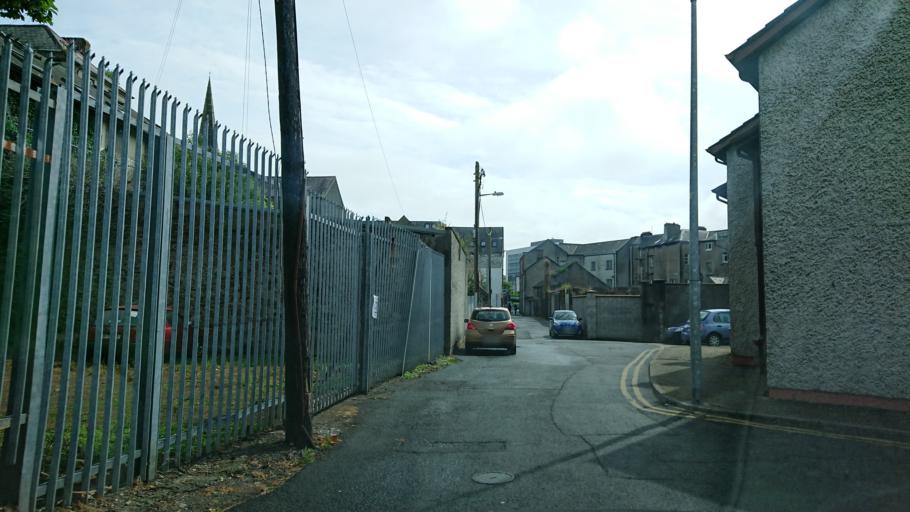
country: IE
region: Munster
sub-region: Waterford
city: Waterford
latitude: 52.2592
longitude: -7.1099
